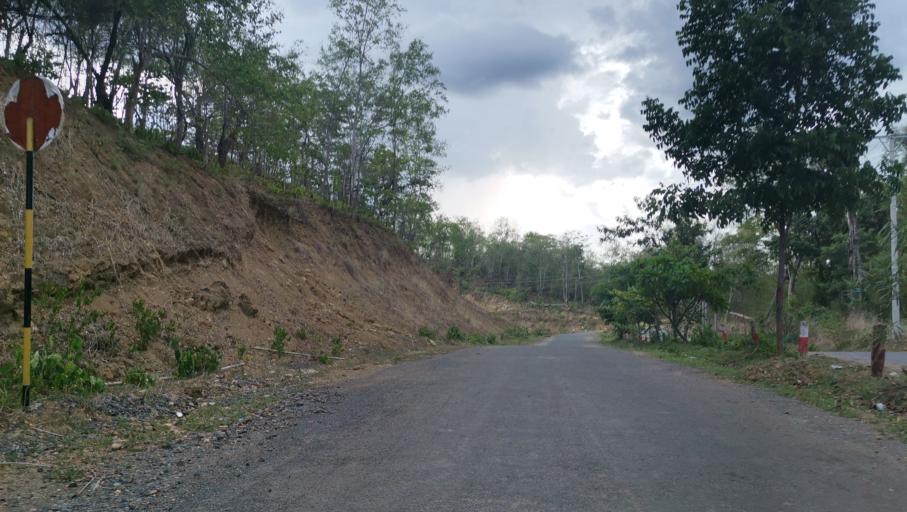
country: MM
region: Magway
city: Minbu
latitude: 20.1048
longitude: 94.5470
